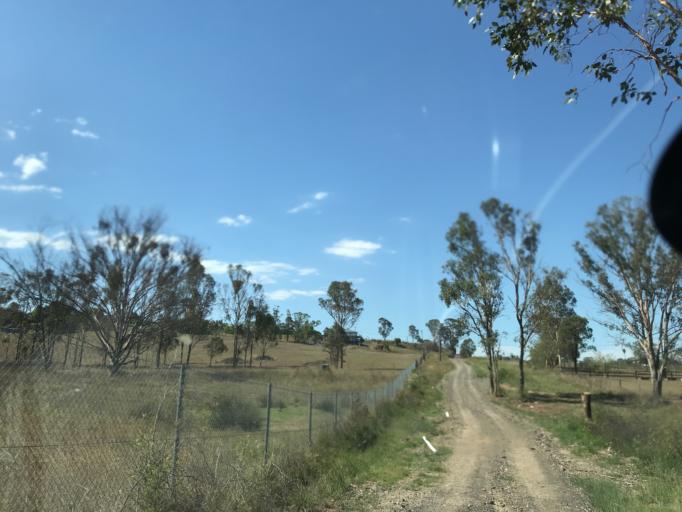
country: AU
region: New South Wales
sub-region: Penrith Municipality
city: Kingswood Park
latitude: -33.7967
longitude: 150.7367
